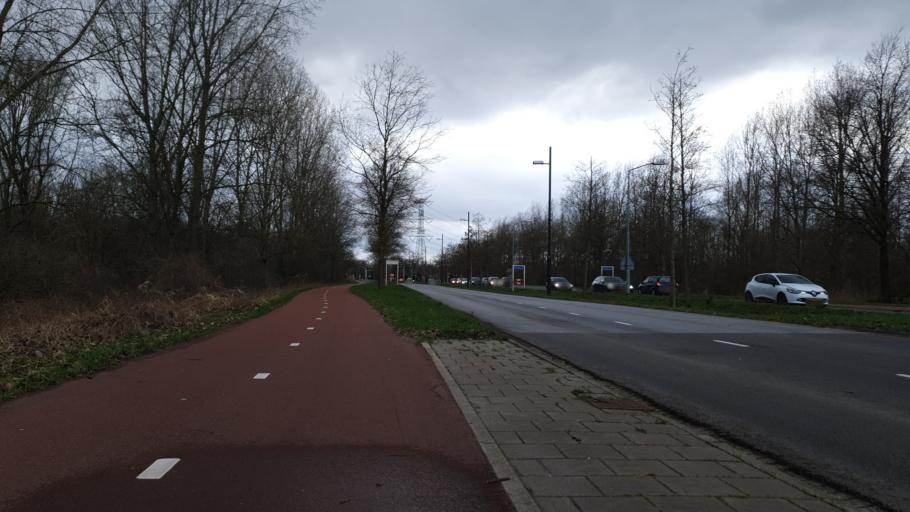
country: NL
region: North Brabant
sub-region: Gemeente Eindhoven
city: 't Hofke
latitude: 51.4674
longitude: 5.5114
